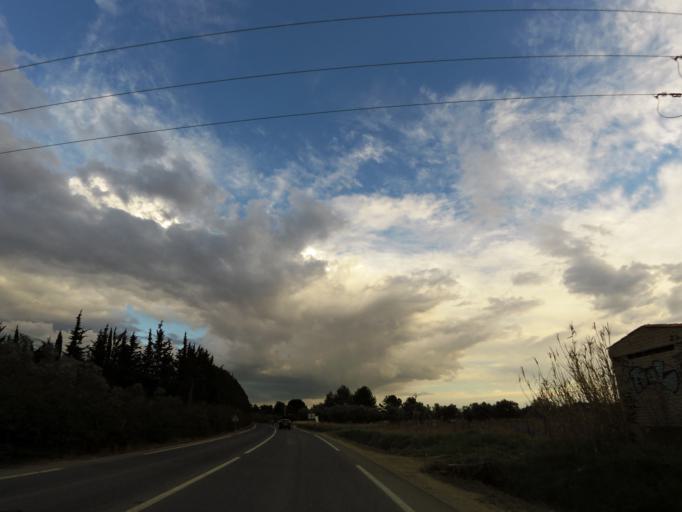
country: FR
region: Languedoc-Roussillon
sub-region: Departement du Gard
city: Codognan
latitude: 43.7327
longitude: 4.2360
